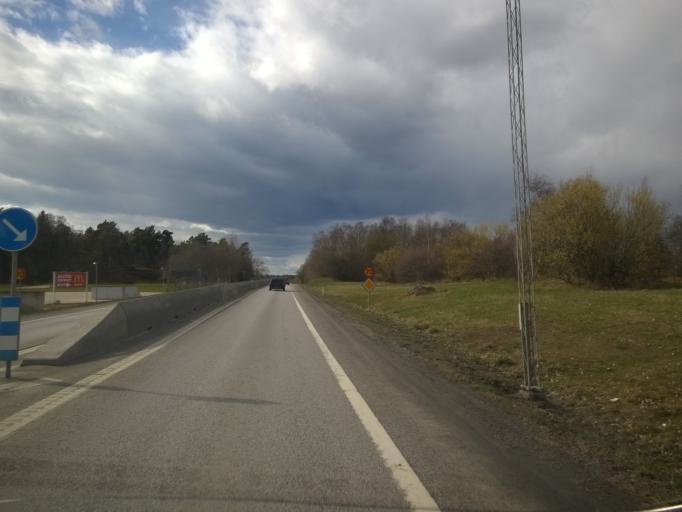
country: SE
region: Stockholm
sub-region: Upplands Vasby Kommun
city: Upplands Vaesby
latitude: 59.4716
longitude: 17.9043
